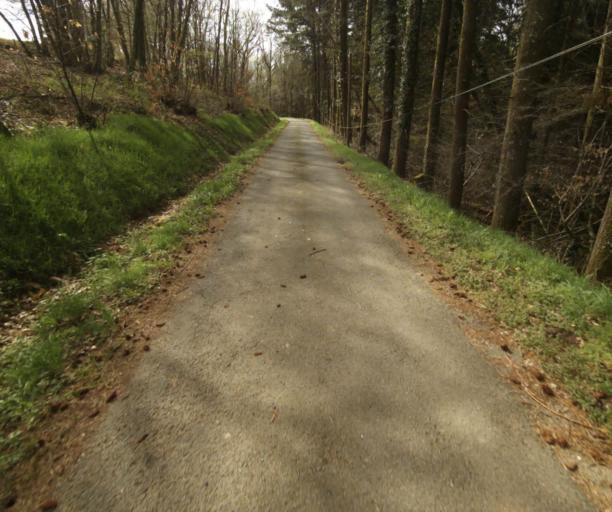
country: FR
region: Limousin
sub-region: Departement de la Correze
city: Correze
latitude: 45.3872
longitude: 1.8144
